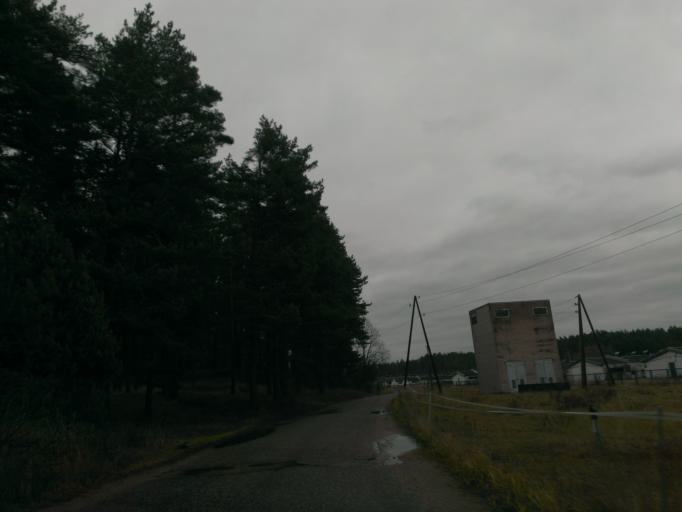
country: LV
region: Adazi
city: Adazi
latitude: 57.0576
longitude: 24.3531
